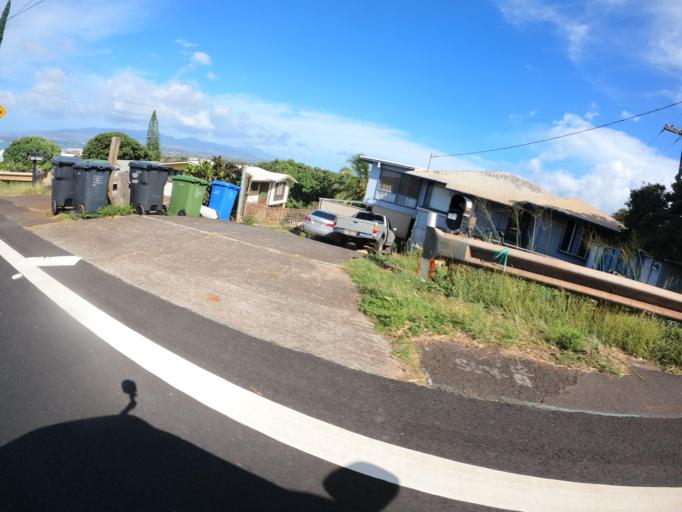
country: US
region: Hawaii
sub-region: Honolulu County
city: Halawa Heights
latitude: 21.3849
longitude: -157.9145
